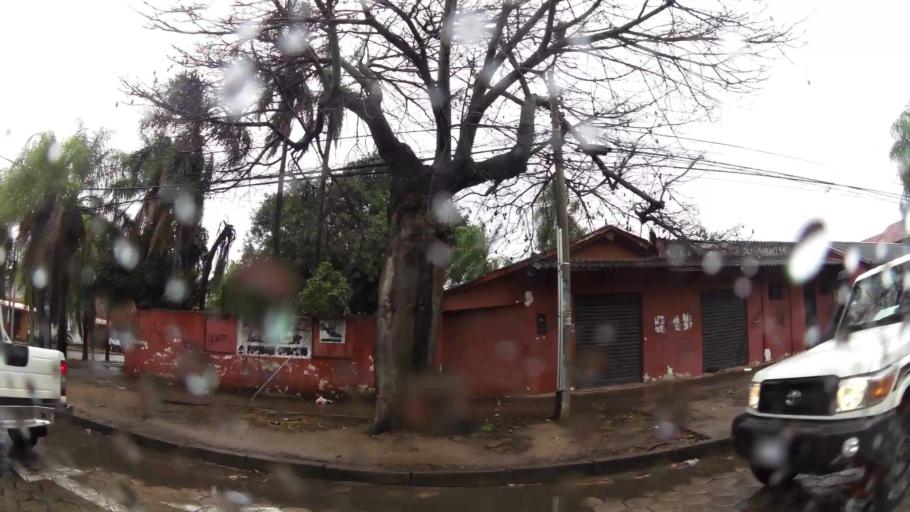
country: BO
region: Santa Cruz
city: Santa Cruz de la Sierra
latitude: -17.8055
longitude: -63.1730
